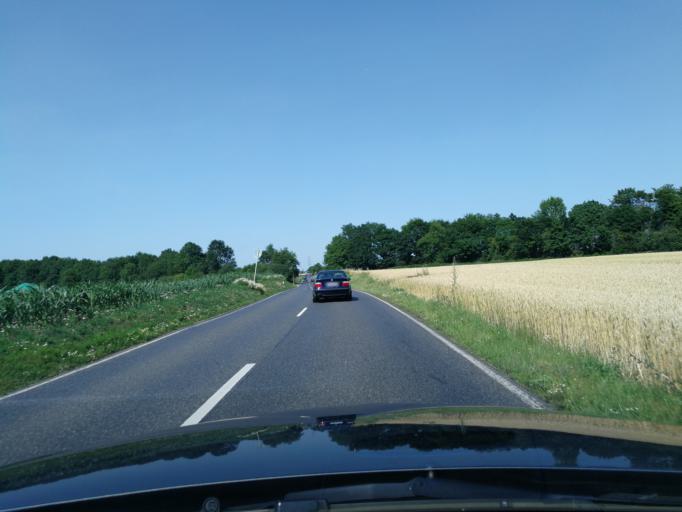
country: DE
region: North Rhine-Westphalia
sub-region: Regierungsbezirk Dusseldorf
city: Neubrueck
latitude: 51.1237
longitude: 6.6693
